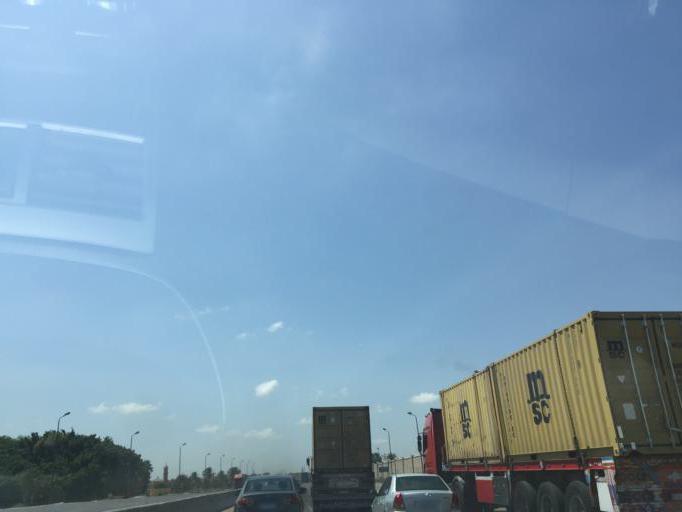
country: EG
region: Alexandria
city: Alexandria
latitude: 30.9714
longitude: 29.8251
